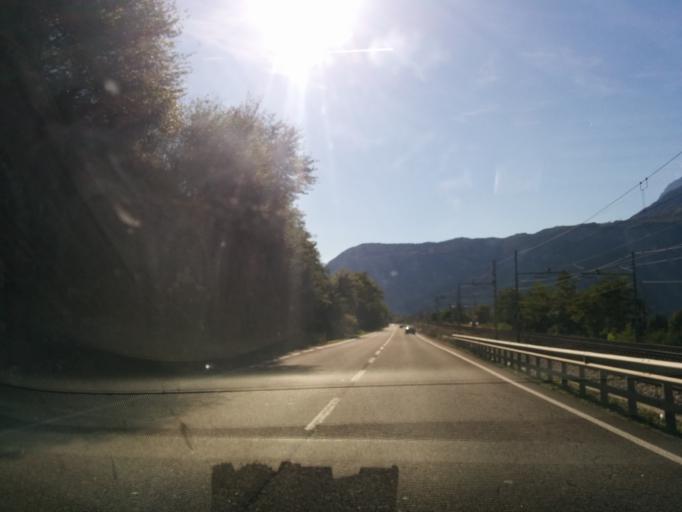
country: IT
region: Trentino-Alto Adige
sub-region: Provincia di Trento
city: Nave San Rocco
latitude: 46.1592
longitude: 11.1068
